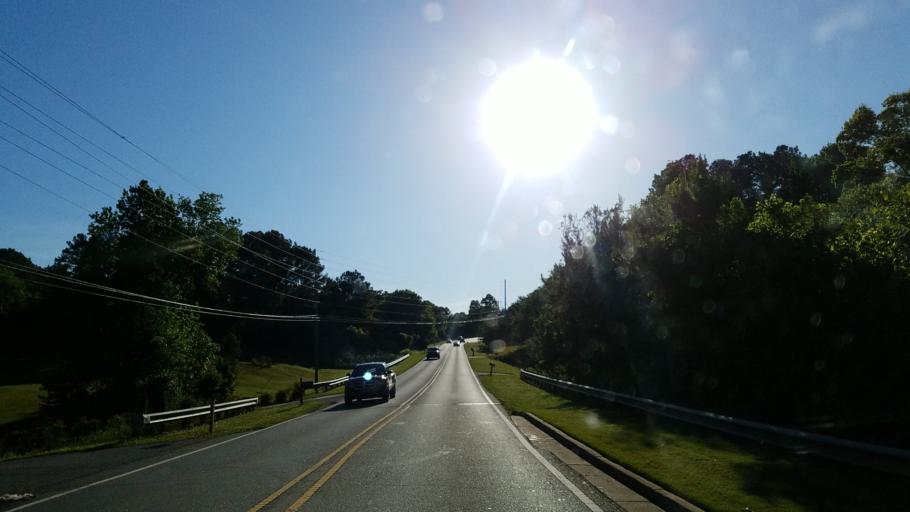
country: US
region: Georgia
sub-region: Cherokee County
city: Holly Springs
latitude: 34.1681
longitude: -84.4552
